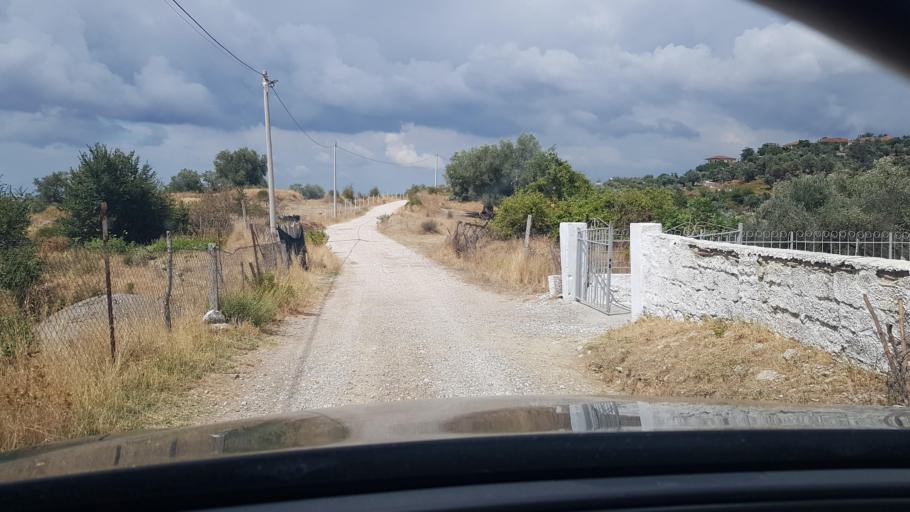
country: AL
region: Tirane
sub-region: Rrethi i Kavajes
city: Golem
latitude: 41.2831
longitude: 19.5466
